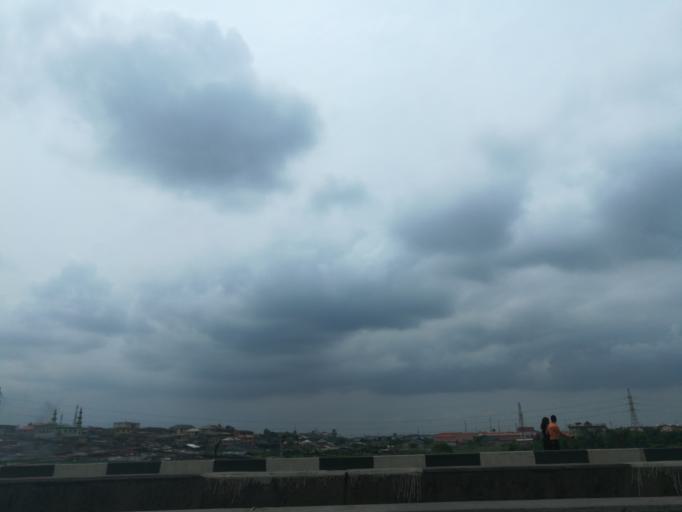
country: NG
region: Lagos
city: Ojota
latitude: 6.5800
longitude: 3.3732
